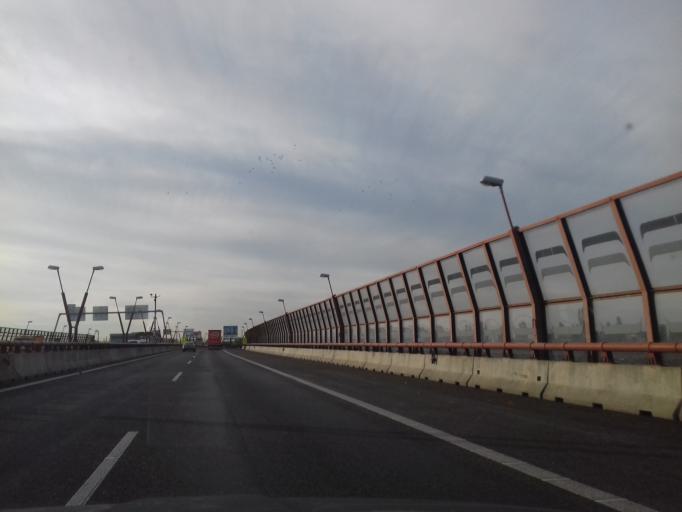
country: SK
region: Bratislavsky
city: Bratislava
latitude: 48.1500
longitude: 17.1810
